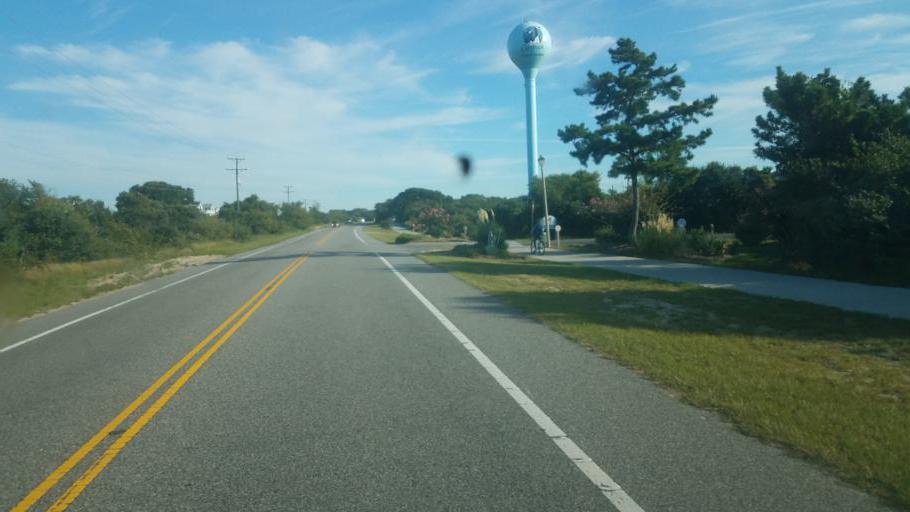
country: US
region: North Carolina
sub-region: Dare County
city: Southern Shores
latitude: 36.3049
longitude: -75.8062
